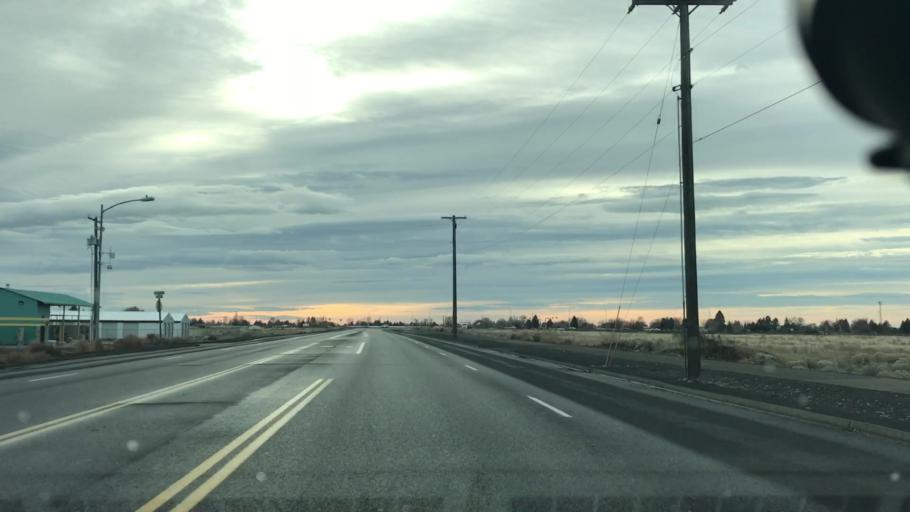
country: US
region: Washington
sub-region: Grant County
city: Cascade Valley
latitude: 47.1608
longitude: -119.3125
